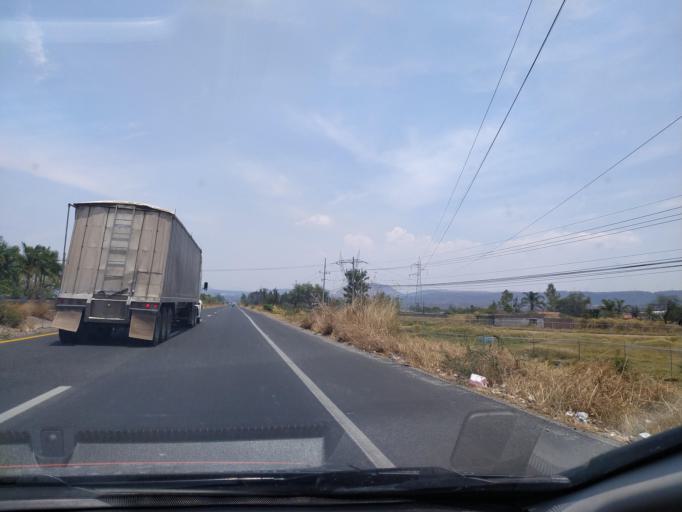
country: MX
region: Jalisco
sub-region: Acatlan de Juarez
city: Villa de los Ninos
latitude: 20.3828
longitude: -103.5929
